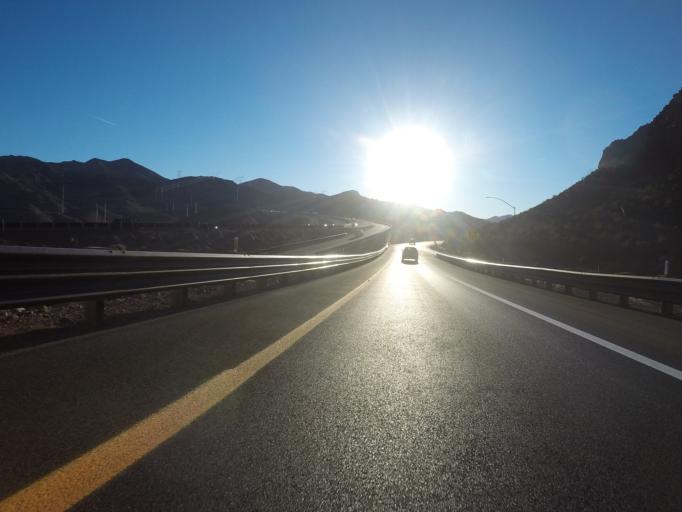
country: US
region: Nevada
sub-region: Clark County
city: Boulder City
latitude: 36.0116
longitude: -114.7755
